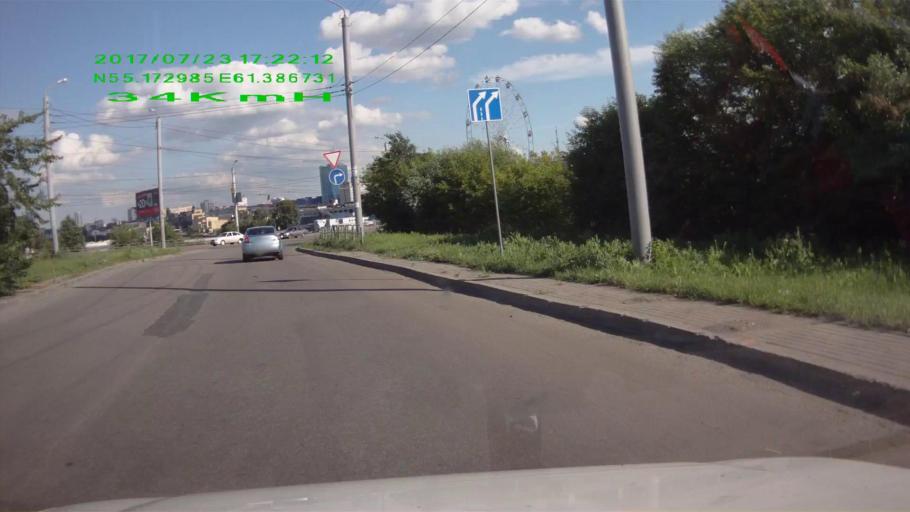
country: RU
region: Chelyabinsk
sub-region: Gorod Chelyabinsk
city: Chelyabinsk
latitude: 55.1727
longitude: 61.3873
